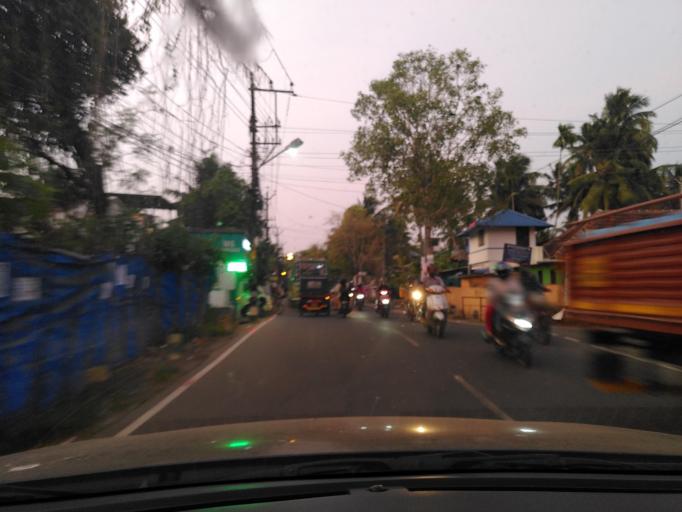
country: IN
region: Kerala
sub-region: Ernakulam
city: Cochin
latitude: 9.9042
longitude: 76.2815
